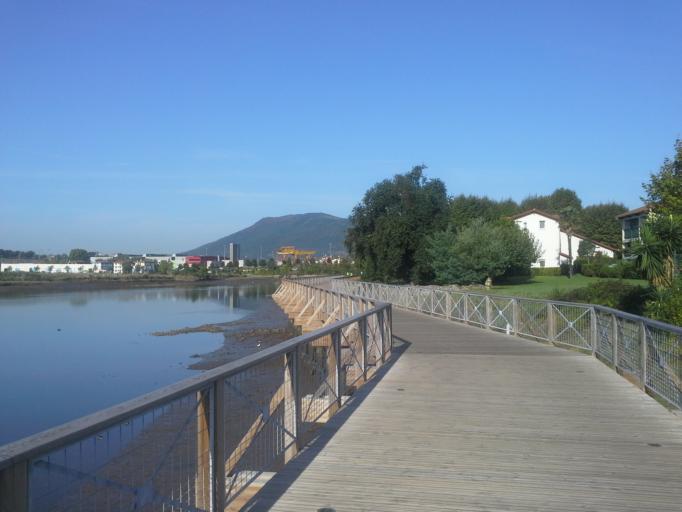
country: ES
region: Basque Country
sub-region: Provincia de Guipuzcoa
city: Irun
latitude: 43.3486
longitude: -1.7796
